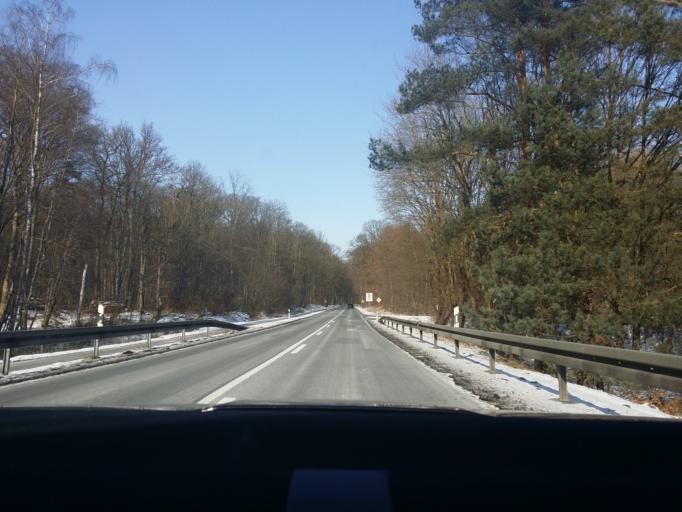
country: DE
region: Mecklenburg-Vorpommern
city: Neustrelitz
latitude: 53.4139
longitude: 13.0415
